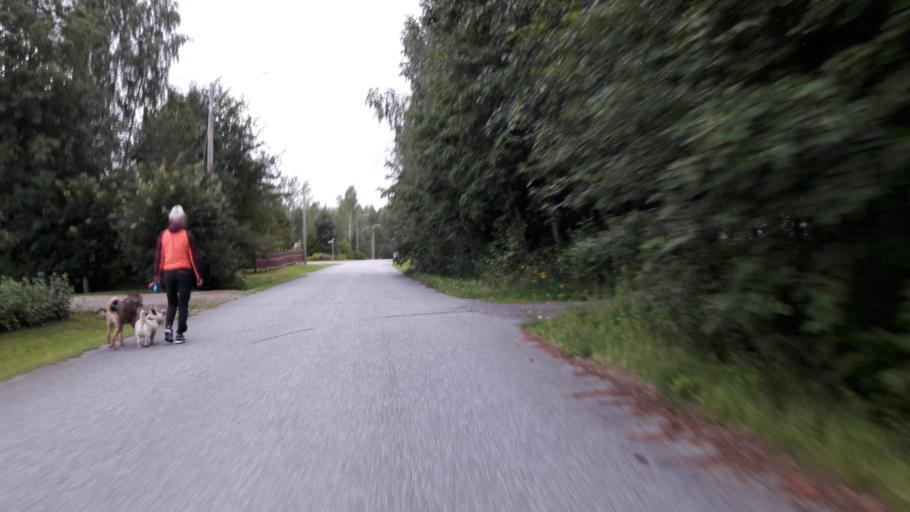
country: FI
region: North Karelia
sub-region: Joensuu
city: Joensuu
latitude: 62.5221
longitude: 29.8587
